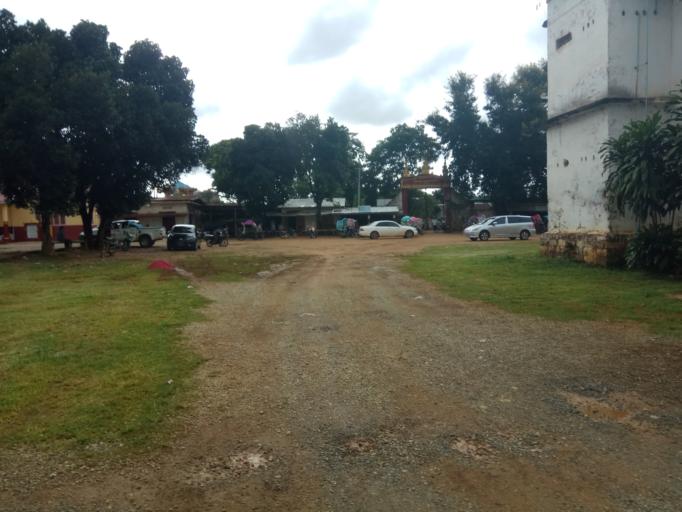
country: MM
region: Shan
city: Lashio
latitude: 22.4932
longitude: 98.3961
